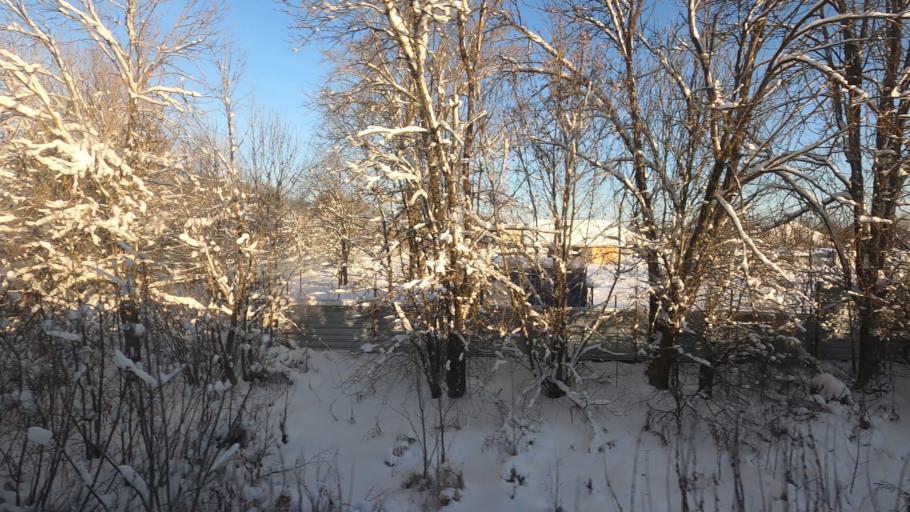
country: RU
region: Moskovskaya
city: Taldom
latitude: 56.7143
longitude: 37.5384
